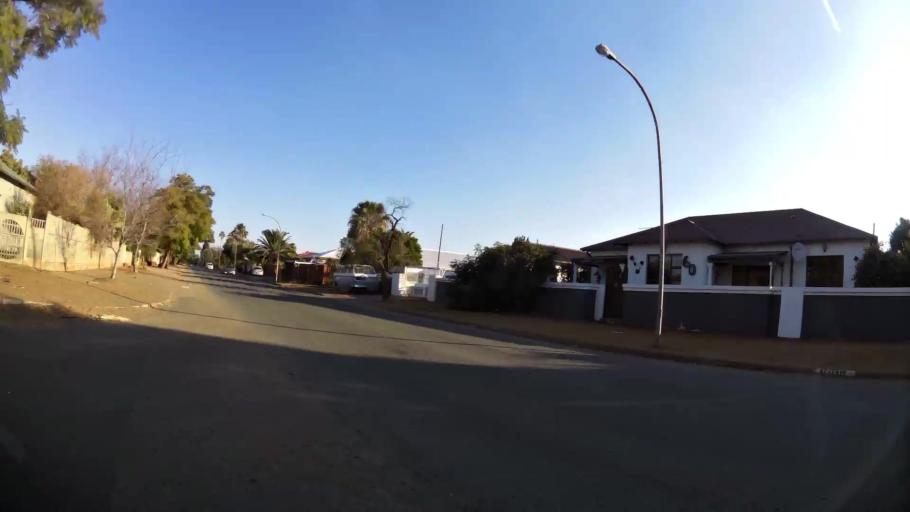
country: ZA
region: Northern Cape
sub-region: Frances Baard District Municipality
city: Kimberley
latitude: -28.7379
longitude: 24.7422
